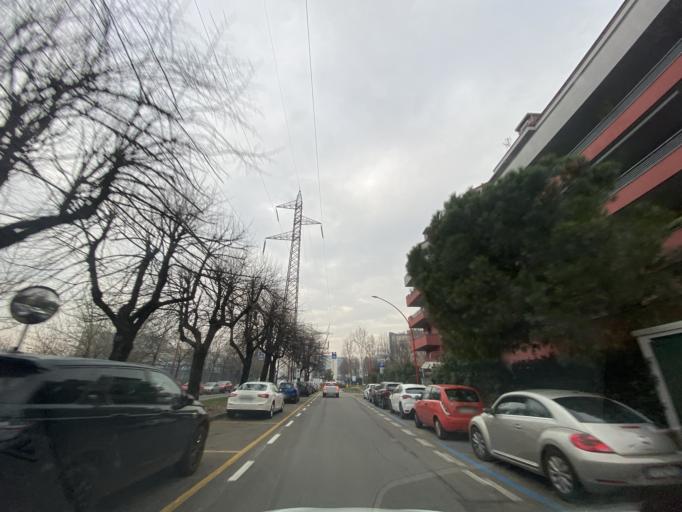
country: IT
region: Lombardy
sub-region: Citta metropolitana di Milano
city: Vimodrone
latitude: 45.5026
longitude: 9.2633
